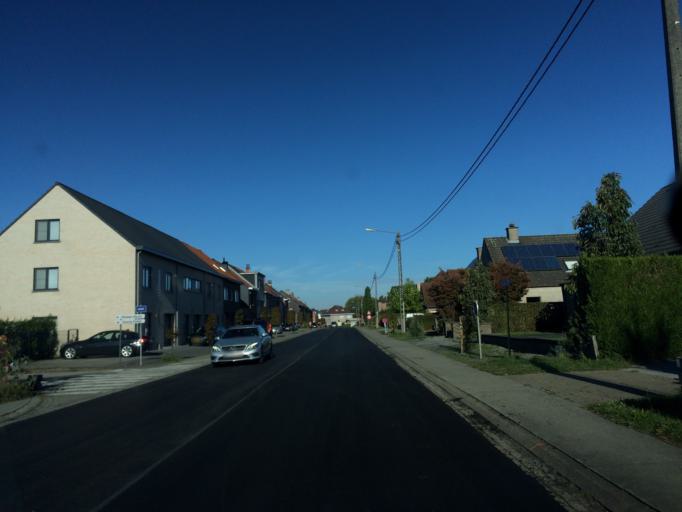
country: BE
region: Flanders
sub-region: Provincie Vlaams-Brabant
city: Merchtem
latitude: 50.9798
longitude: 4.2303
